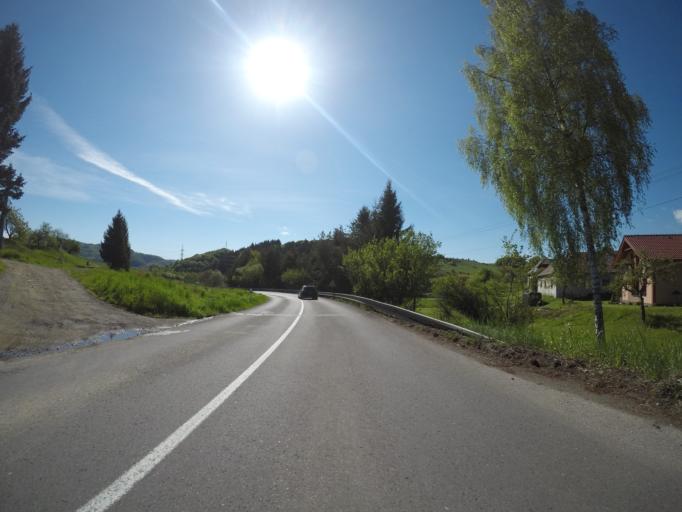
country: SK
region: Banskobystricky
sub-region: Okres Banska Bystrica
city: Banska Stiavnica
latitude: 48.4723
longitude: 18.9176
